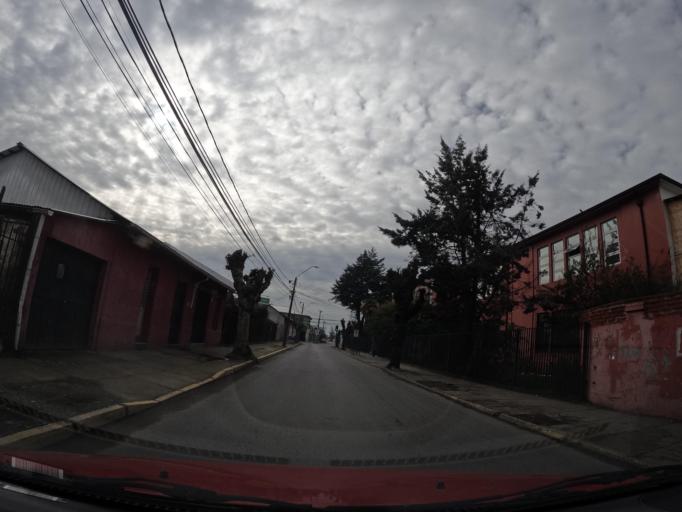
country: CL
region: Maule
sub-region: Provincia de Linares
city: Linares
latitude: -35.8500
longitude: -71.5893
